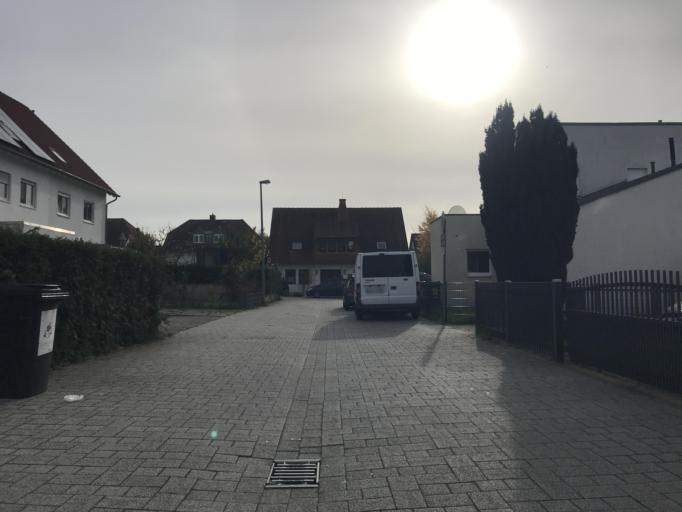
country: DE
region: Rheinland-Pfalz
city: Mainz
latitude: 50.0175
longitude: 8.2996
